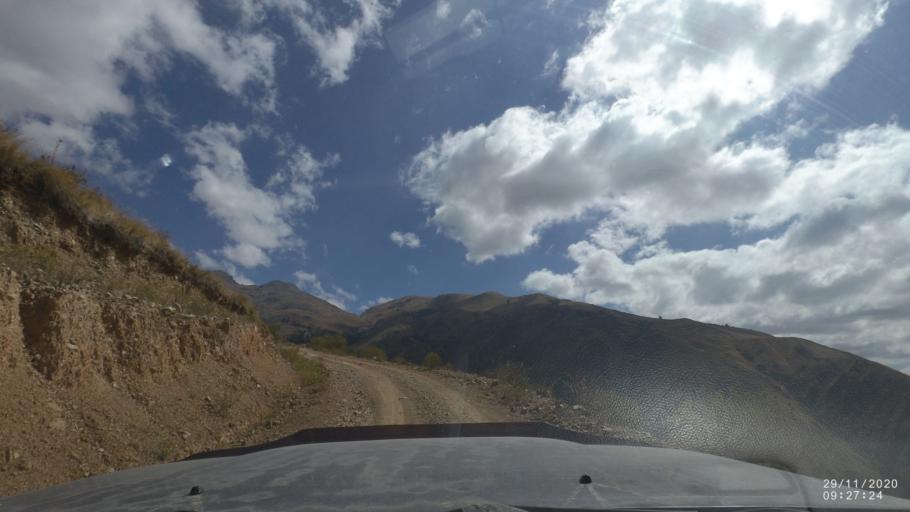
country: BO
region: Cochabamba
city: Cochabamba
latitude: -17.3181
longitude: -66.1862
